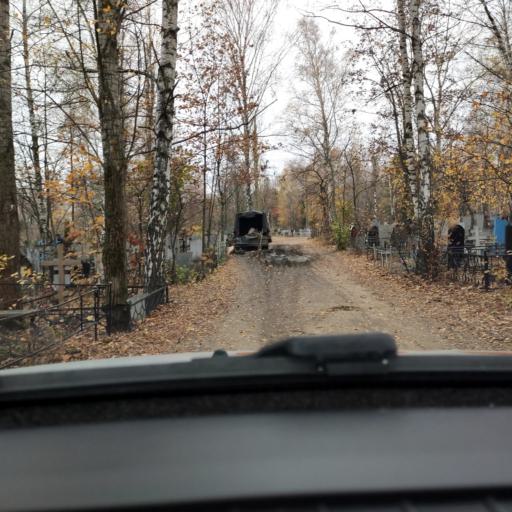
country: RU
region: Voronezj
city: Pridonskoy
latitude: 51.6693
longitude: 39.1090
